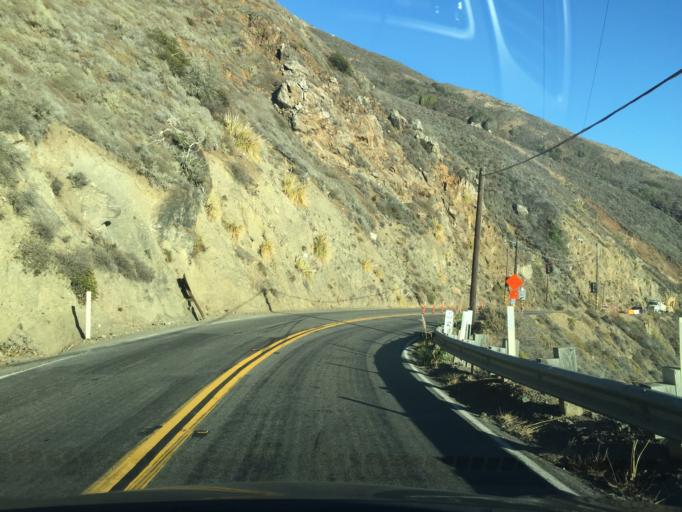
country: US
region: California
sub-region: San Luis Obispo County
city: Cambria
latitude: 35.7930
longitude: -121.3414
